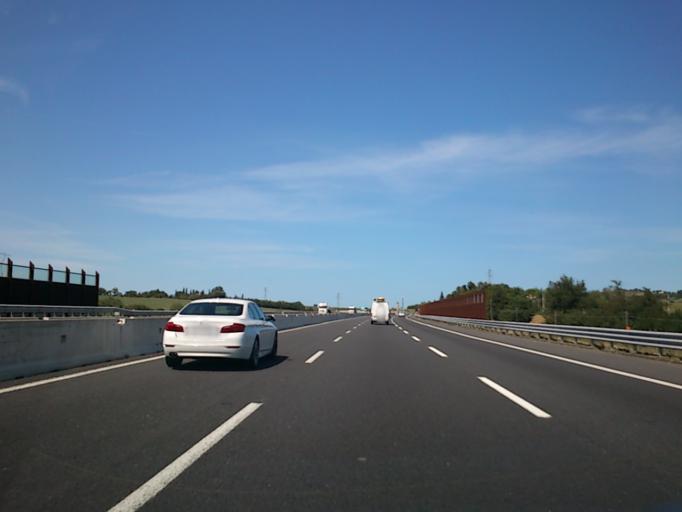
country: IT
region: The Marches
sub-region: Provincia di Pesaro e Urbino
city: Borgo Santa Maria
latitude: 43.9151
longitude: 12.8174
